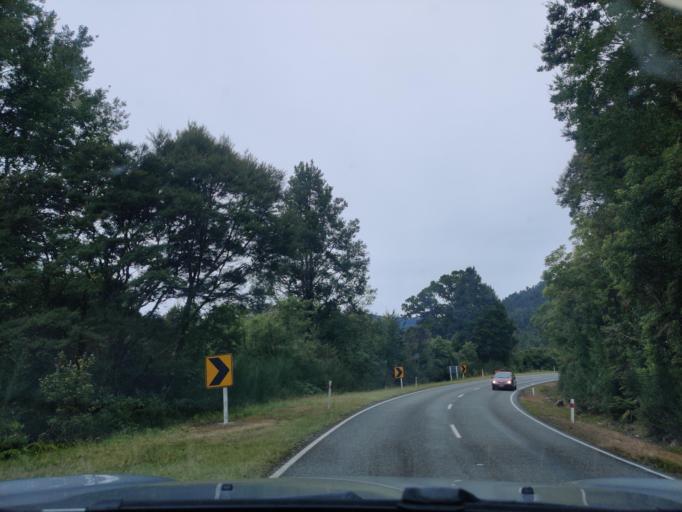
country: NZ
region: West Coast
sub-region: Buller District
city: Westport
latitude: -41.8475
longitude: 171.7874
